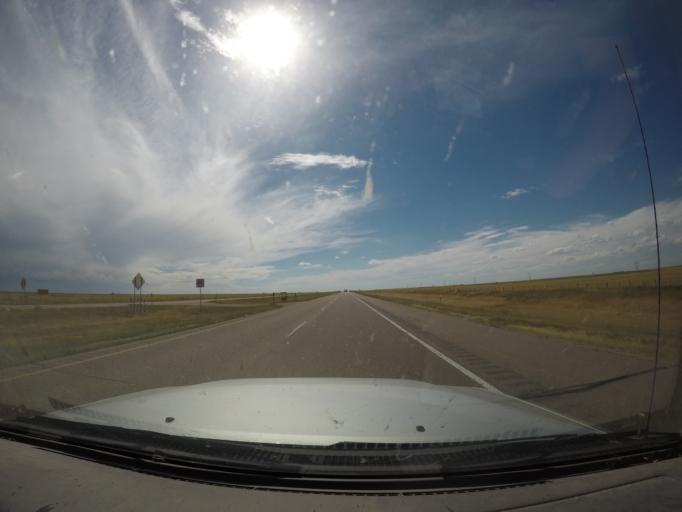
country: US
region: Colorado
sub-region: Sedgwick County
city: Julesburg
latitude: 41.0491
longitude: -102.3538
